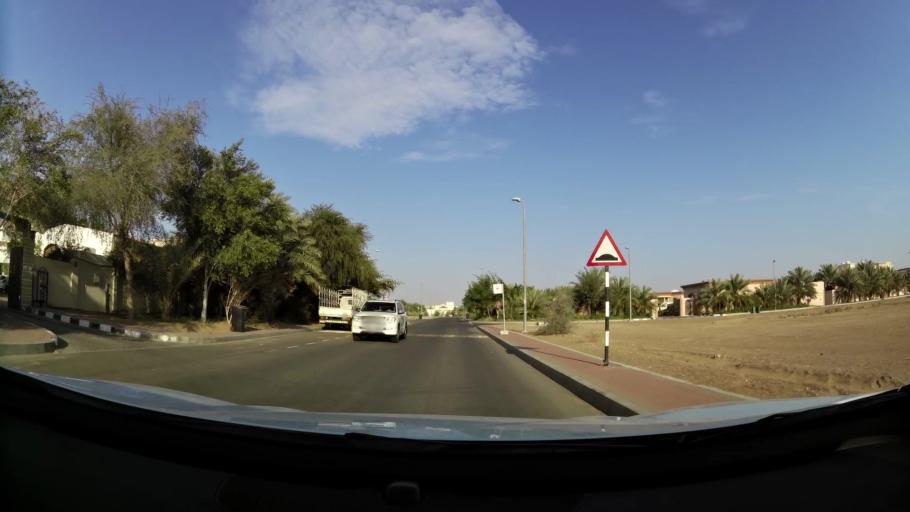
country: AE
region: Abu Dhabi
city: Al Ain
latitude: 24.0793
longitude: 55.8408
